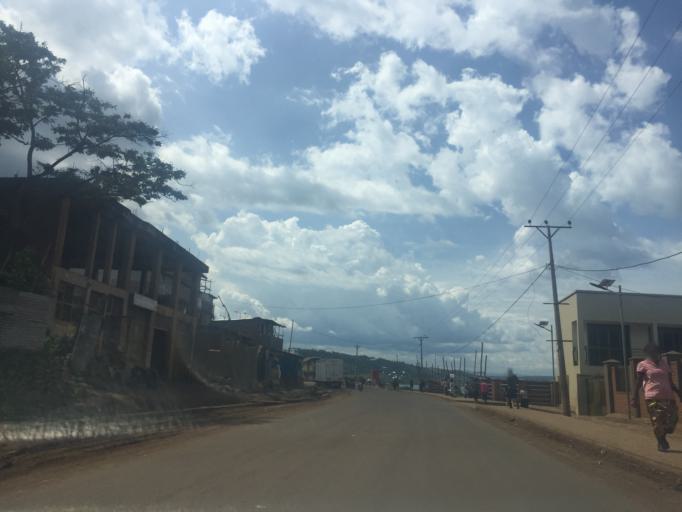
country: CD
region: South Kivu
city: Bukavu
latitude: -2.4854
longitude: 28.8461
